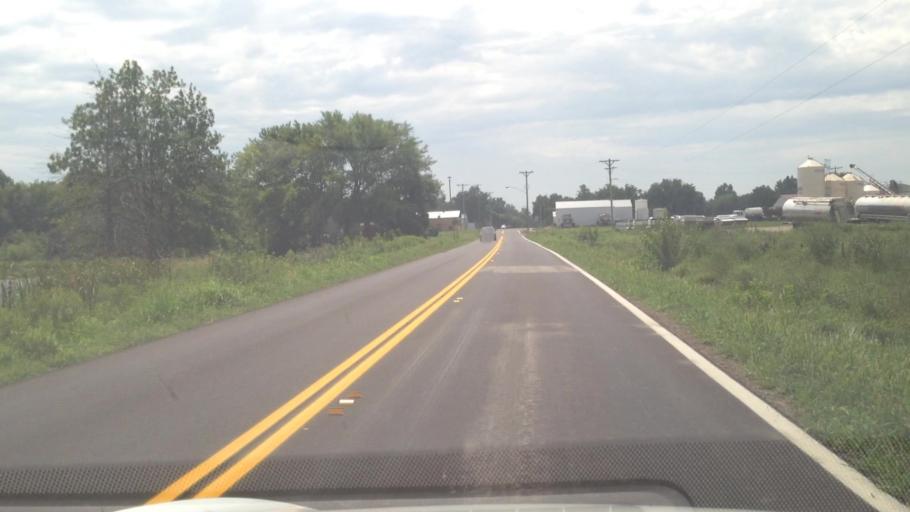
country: US
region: Kansas
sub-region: Crawford County
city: Girard
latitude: 37.6658
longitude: -94.9697
